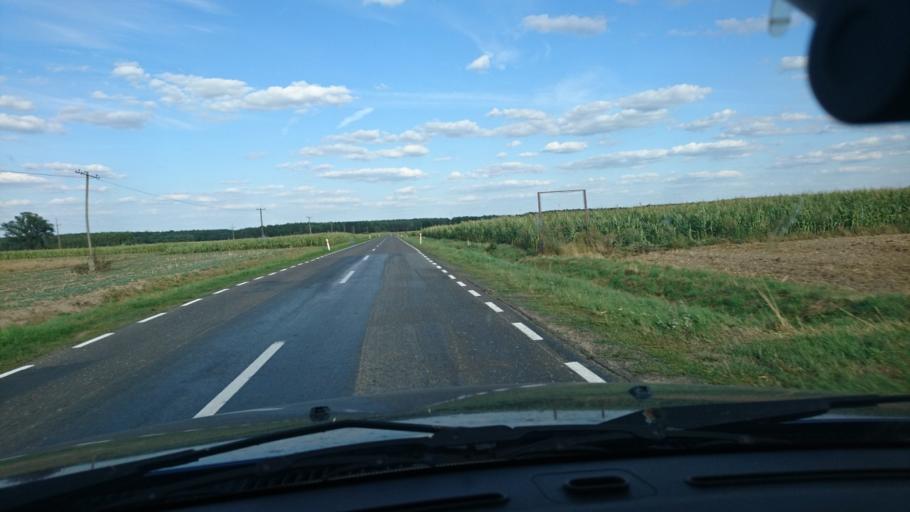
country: PL
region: Greater Poland Voivodeship
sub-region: Powiat krotoszynski
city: Sulmierzyce
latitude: 51.6051
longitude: 17.5570
